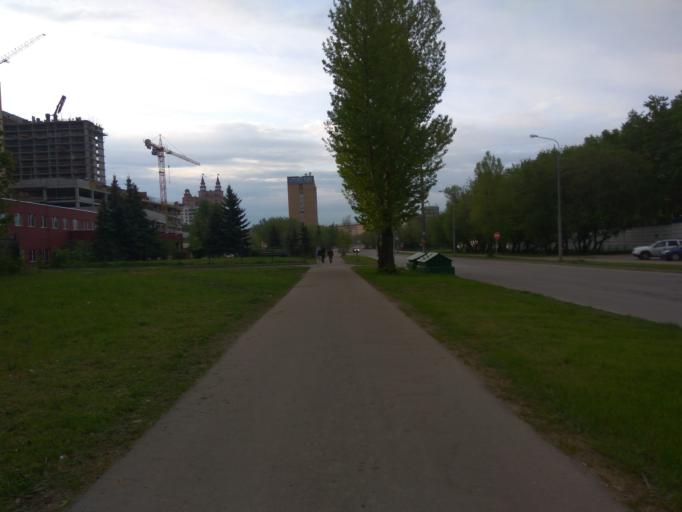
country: RU
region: Moscow
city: Sokol
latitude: 55.7841
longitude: 37.5003
